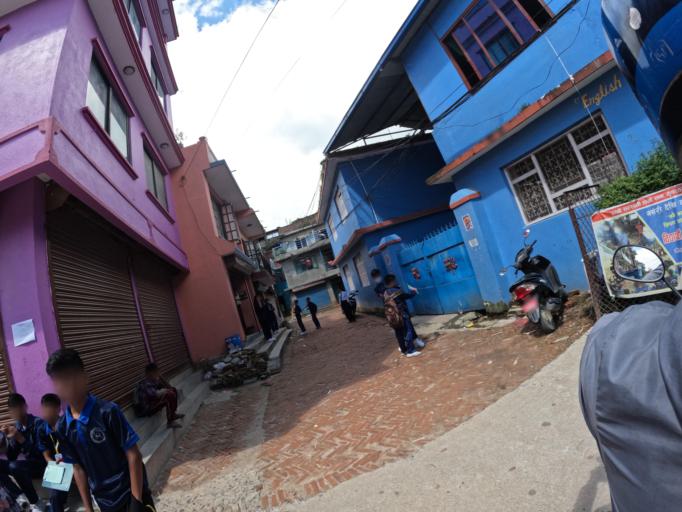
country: NP
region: Central Region
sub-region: Bagmati Zone
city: Kathmandu
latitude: 27.7664
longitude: 85.3312
